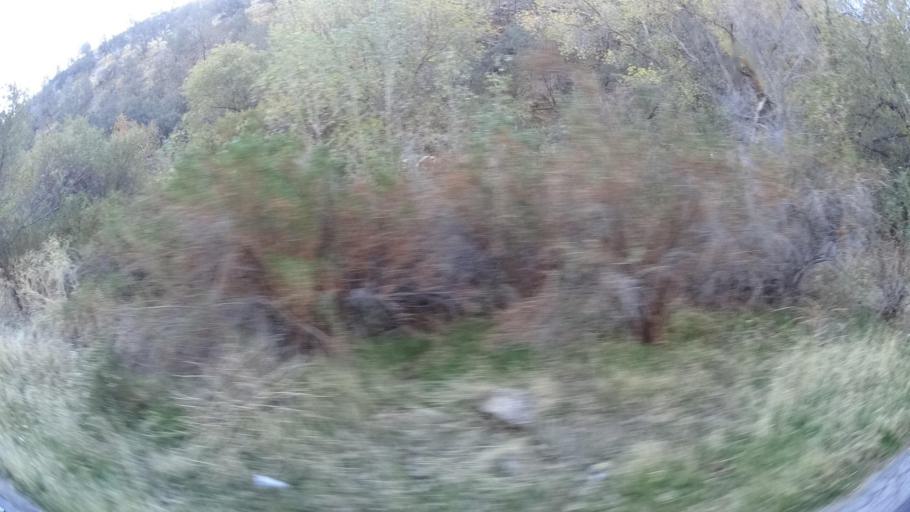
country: US
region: California
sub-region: Kern County
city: Bear Valley Springs
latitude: 35.3110
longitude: -118.5679
